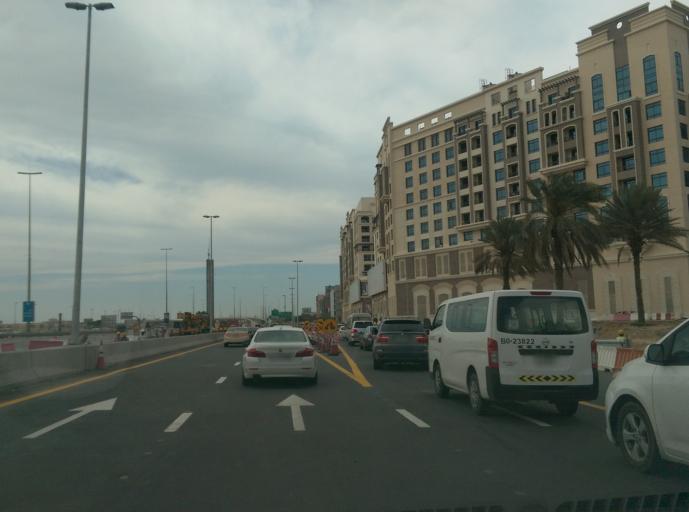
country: AE
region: Ash Shariqah
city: Sharjah
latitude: 25.2302
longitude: 55.3145
